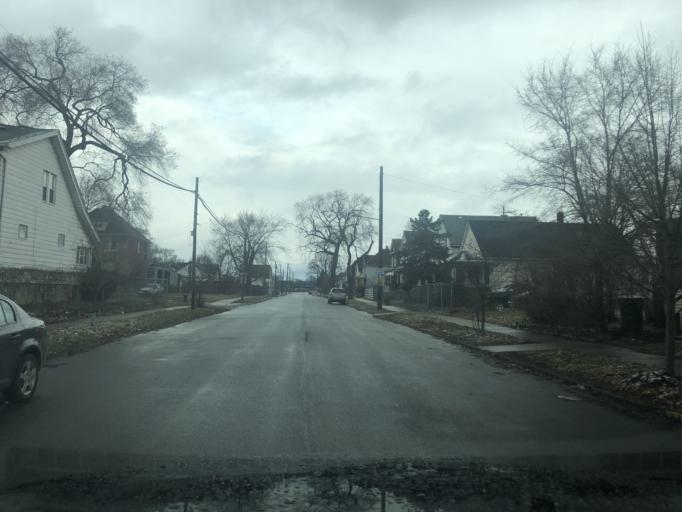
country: US
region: Michigan
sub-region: Wayne County
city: River Rouge
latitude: 42.3074
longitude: -83.1135
